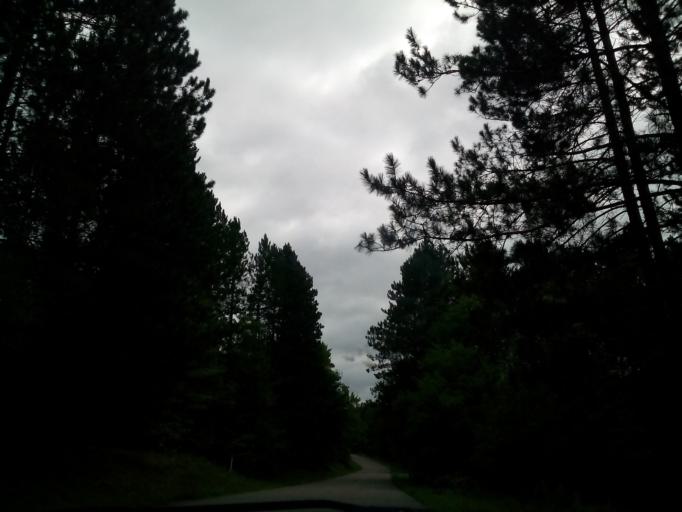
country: US
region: Wisconsin
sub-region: Menominee County
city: Legend Lake
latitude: 45.3257
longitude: -88.5277
